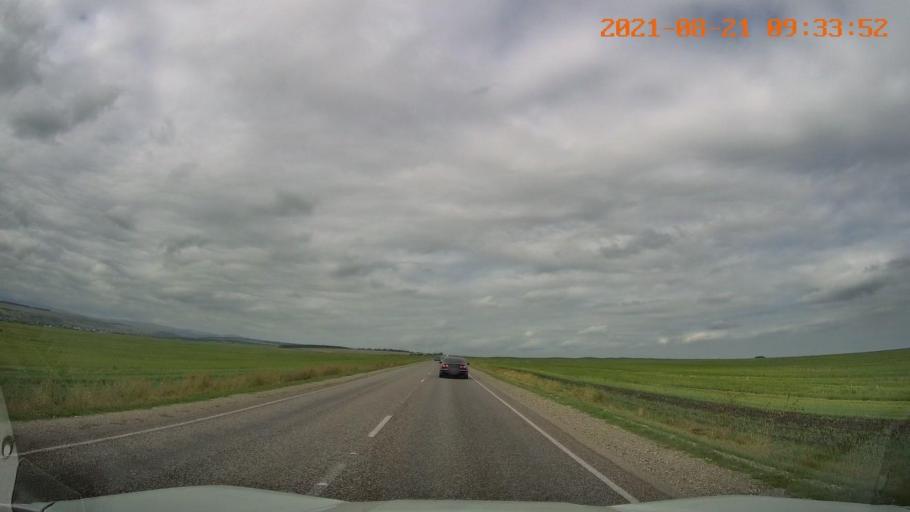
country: RU
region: Stavropol'skiy
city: Yutsa
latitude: 43.9927
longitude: 42.9821
